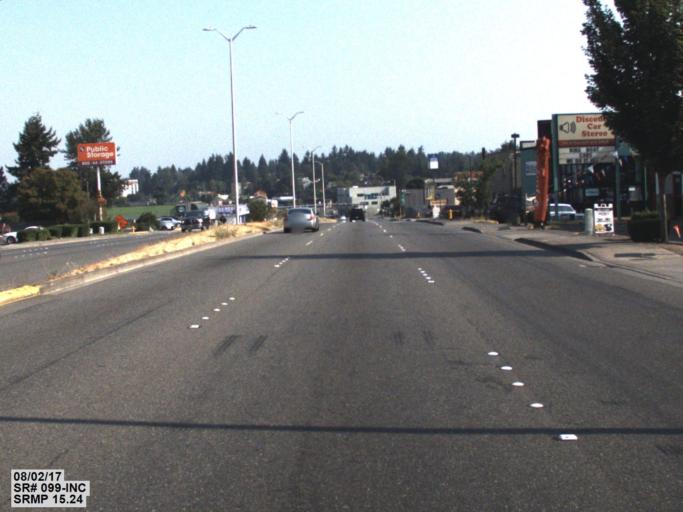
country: US
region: Washington
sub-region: King County
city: Des Moines
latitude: 47.3900
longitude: -122.2955
